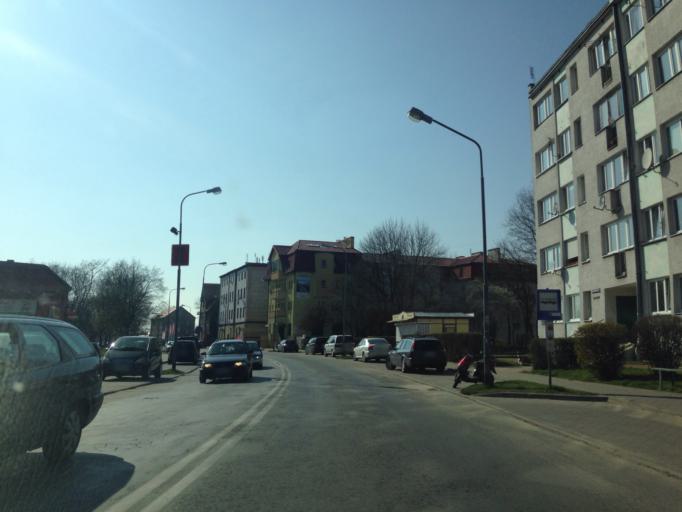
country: PL
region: Lower Silesian Voivodeship
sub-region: Powiat olesnicki
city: Olesnica
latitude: 51.2125
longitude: 17.3817
